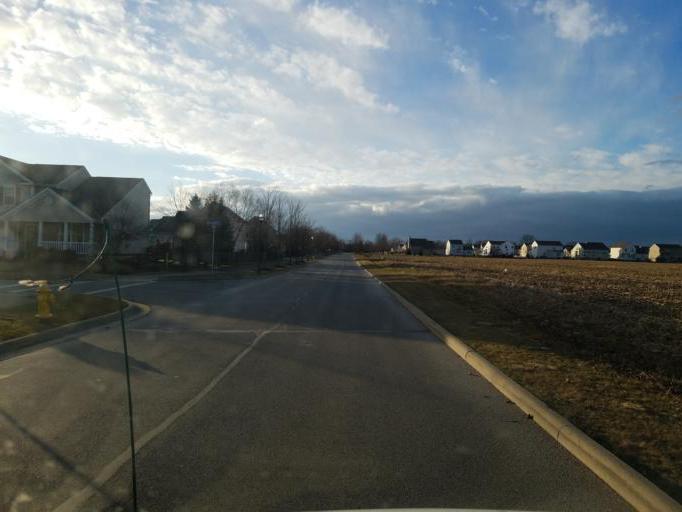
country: US
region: Ohio
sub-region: Delaware County
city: Delaware
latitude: 40.3210
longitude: -83.1088
